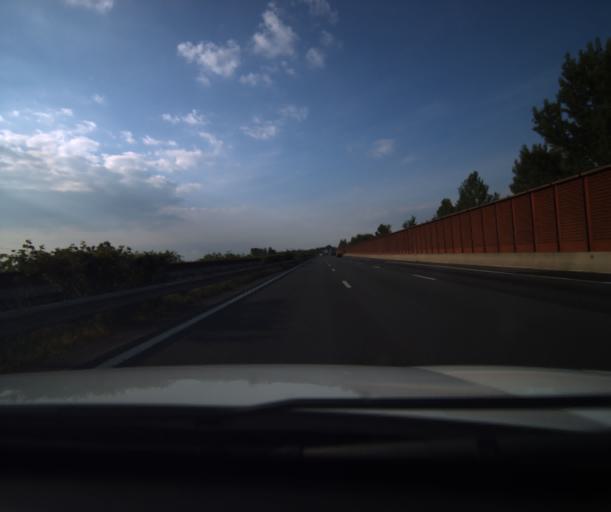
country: FR
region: Midi-Pyrenees
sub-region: Departement de la Haute-Garonne
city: Bouloc
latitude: 43.7712
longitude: 1.3845
